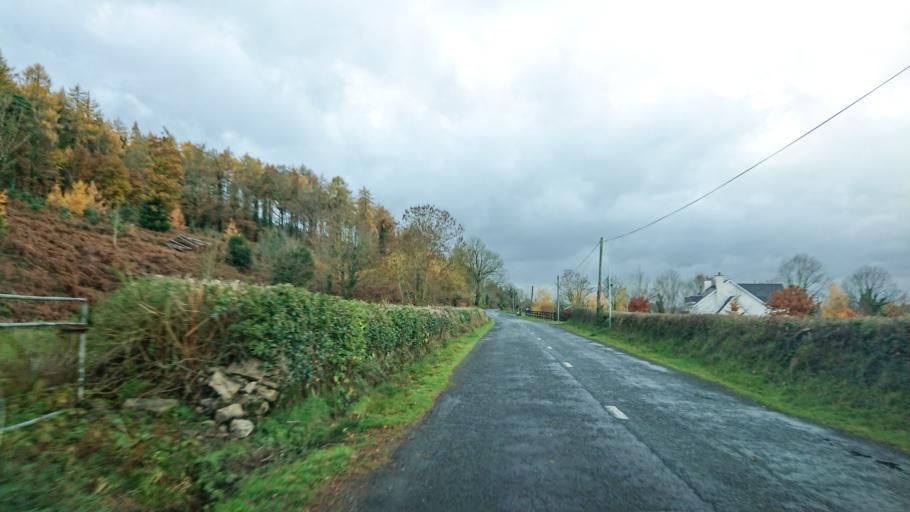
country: IE
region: Munster
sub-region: South Tipperary
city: Cluain Meala
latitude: 52.3563
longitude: -7.6165
